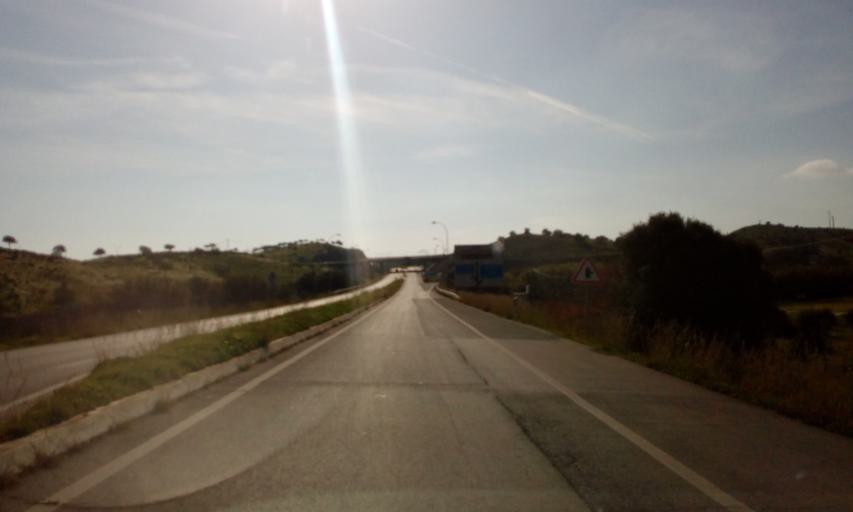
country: PT
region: Faro
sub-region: Castro Marim
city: Castro Marim
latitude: 37.2344
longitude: -7.4475
